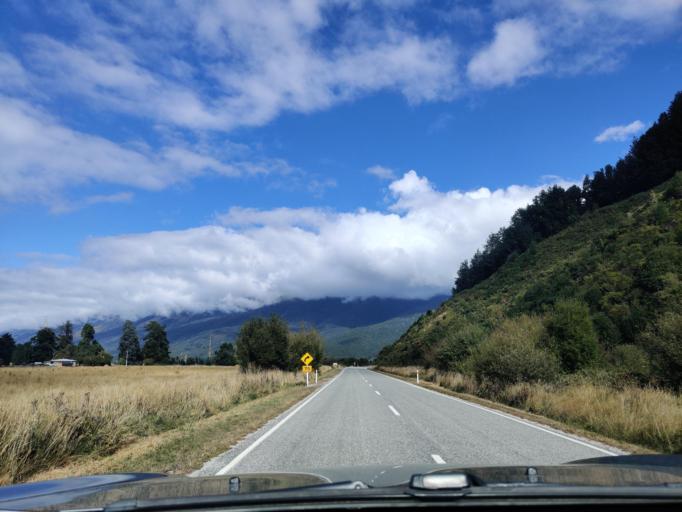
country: NZ
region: Otago
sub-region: Queenstown-Lakes District
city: Queenstown
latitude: -44.7974
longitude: 168.3775
